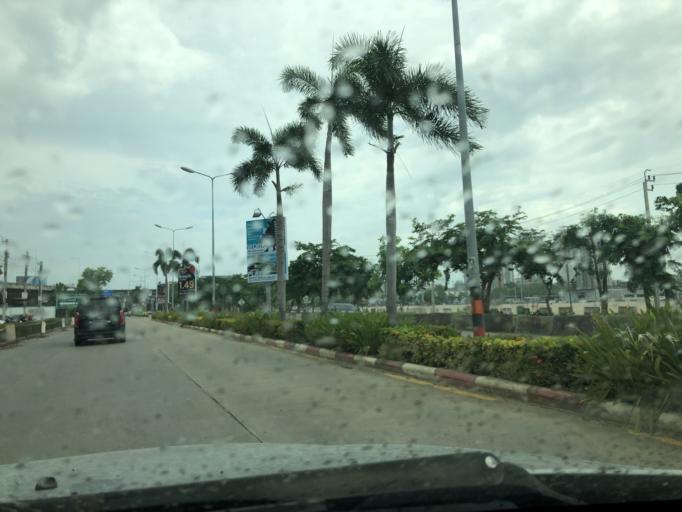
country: TH
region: Bangkok
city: Don Mueang
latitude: 13.9198
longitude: 100.5460
